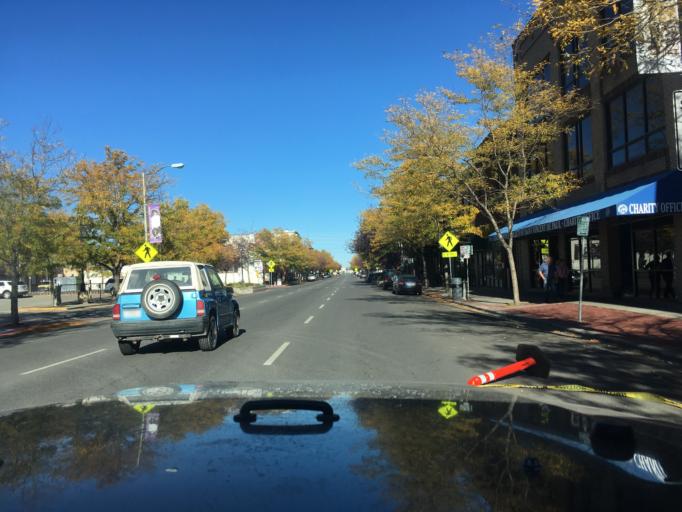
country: US
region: Montana
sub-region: Yellowstone County
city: Billings
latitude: 45.7820
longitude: -108.5033
